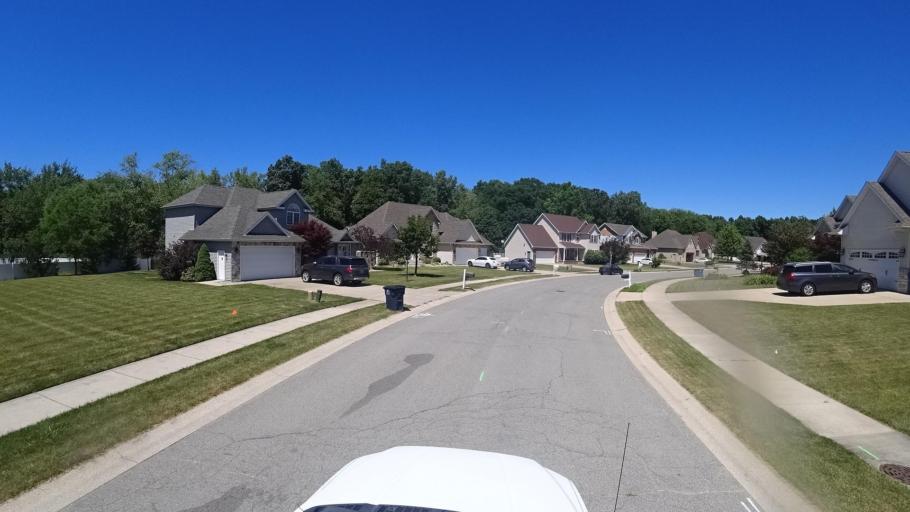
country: US
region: Indiana
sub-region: Porter County
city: Porter
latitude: 41.6338
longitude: -87.0750
